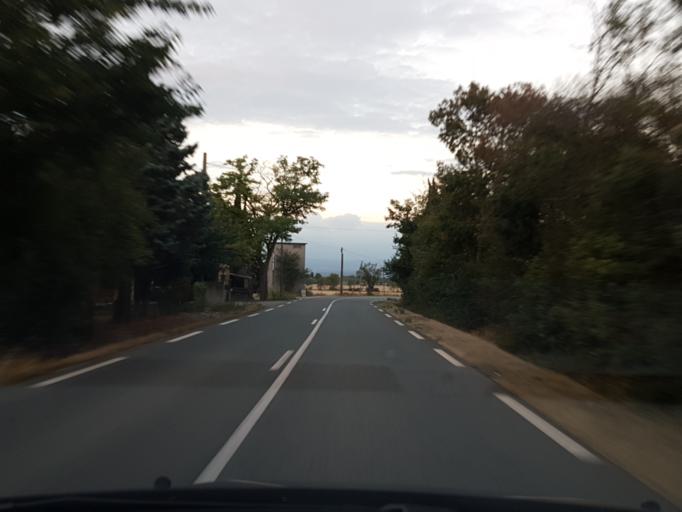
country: FR
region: Languedoc-Roussillon
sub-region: Departement de l'Aude
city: Bram
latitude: 43.2106
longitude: 2.0687
